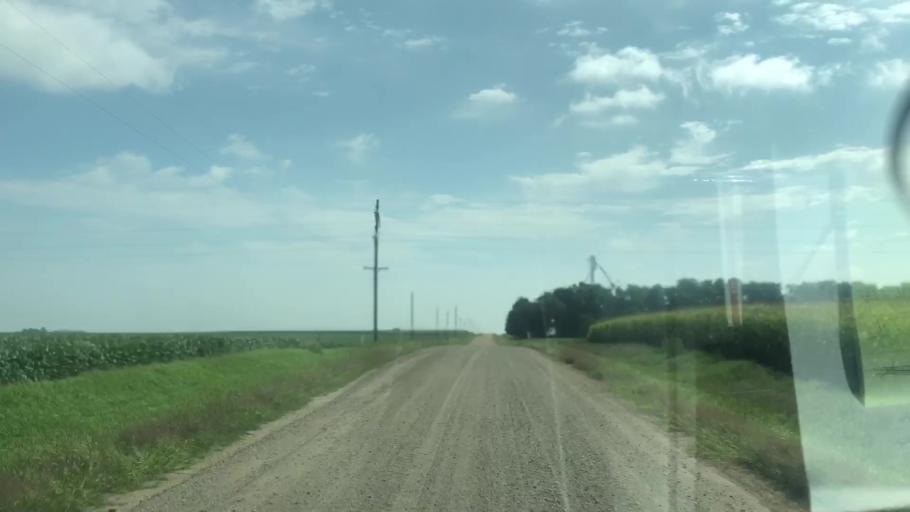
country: US
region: Iowa
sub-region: Lyon County
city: George
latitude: 43.2153
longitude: -95.9834
